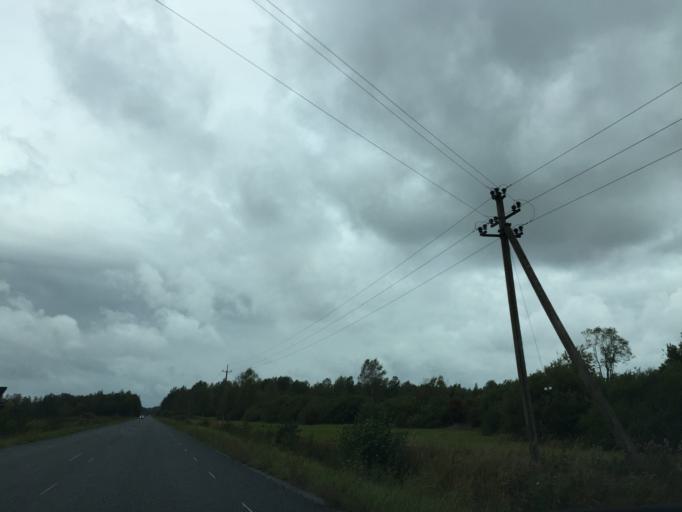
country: LV
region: Salacgrivas
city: Ainazi
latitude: 57.9696
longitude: 24.4451
